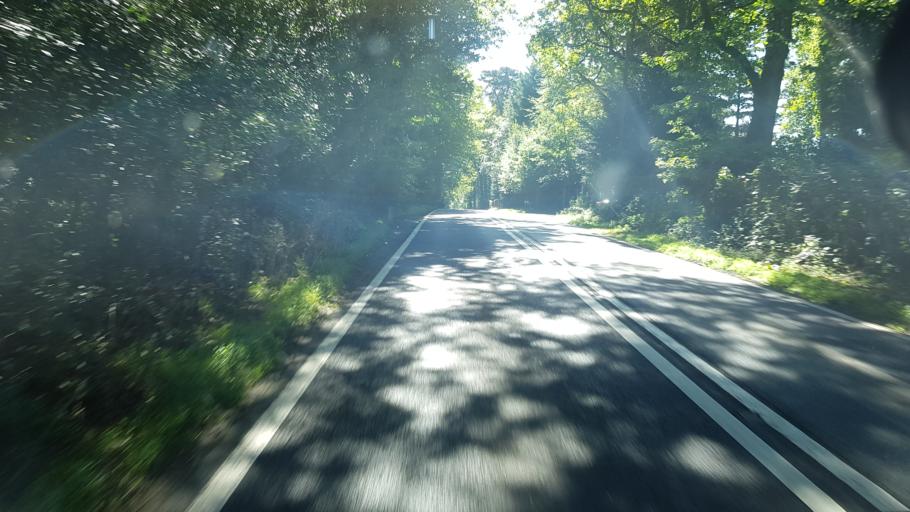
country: GB
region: England
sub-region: Kent
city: Kings Hill
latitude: 51.2751
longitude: 0.3554
